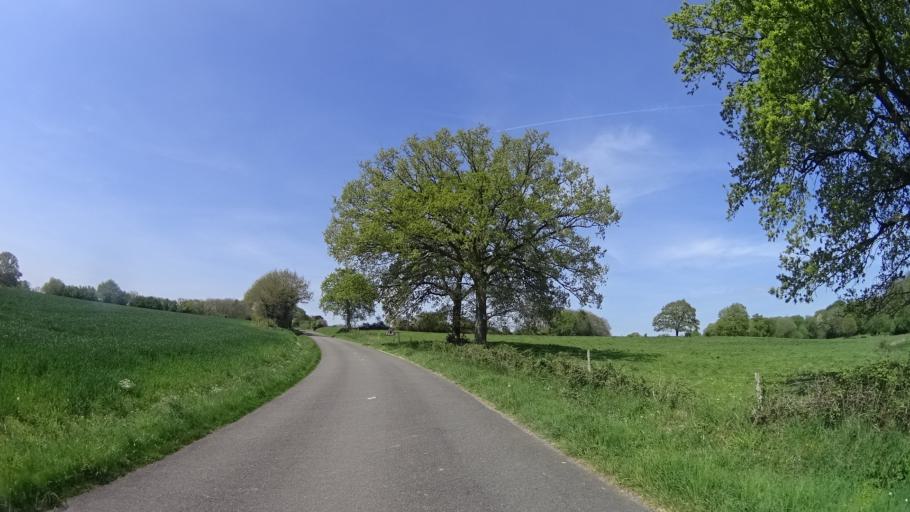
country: FR
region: Pays de la Loire
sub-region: Departement de la Loire-Atlantique
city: Fegreac
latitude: 47.5931
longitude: -2.0498
